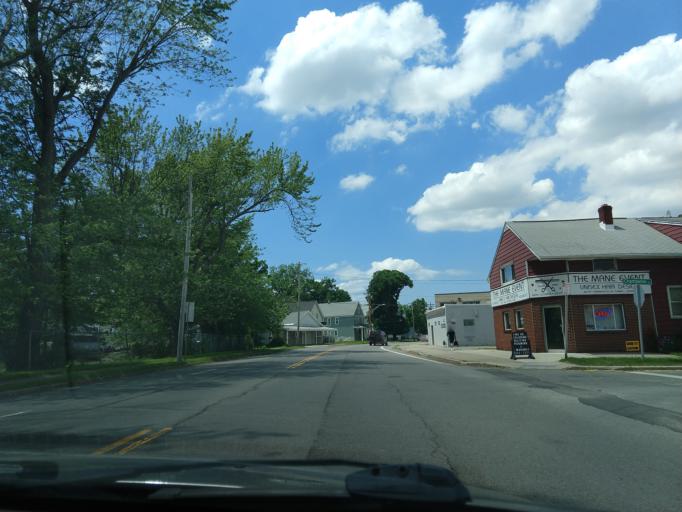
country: US
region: New York
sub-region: Erie County
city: West Seneca
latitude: 42.8488
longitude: -78.8023
